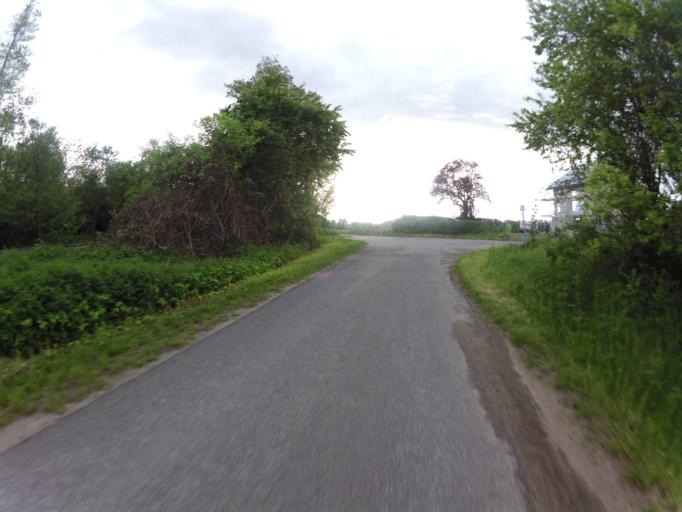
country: DE
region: Bavaria
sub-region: Regierungsbezirk Unterfranken
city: Volkach
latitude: 49.8686
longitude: 10.2344
